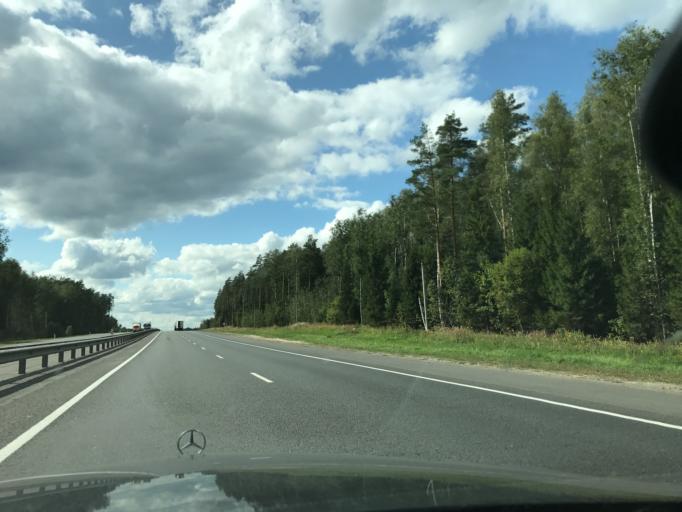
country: RU
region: Vladimir
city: Orgtrud
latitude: 56.1035
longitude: 40.6775
